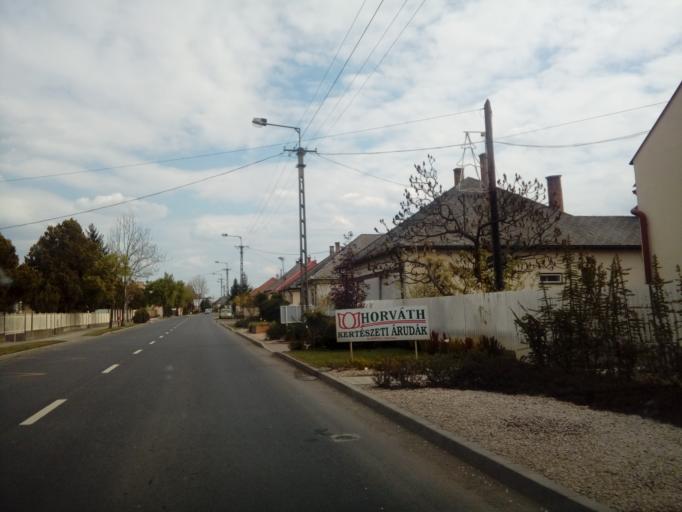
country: HU
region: Szabolcs-Szatmar-Bereg
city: Nagykallo
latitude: 47.8784
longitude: 21.8329
